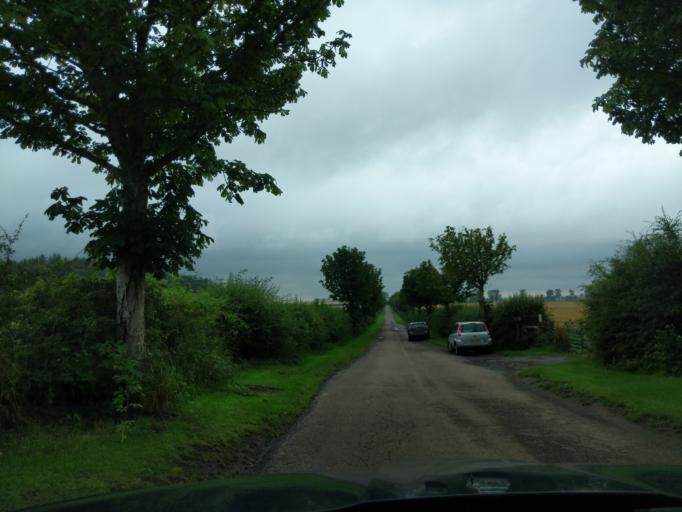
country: GB
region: England
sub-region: Northumberland
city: Ford
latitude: 55.6767
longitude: -2.1089
